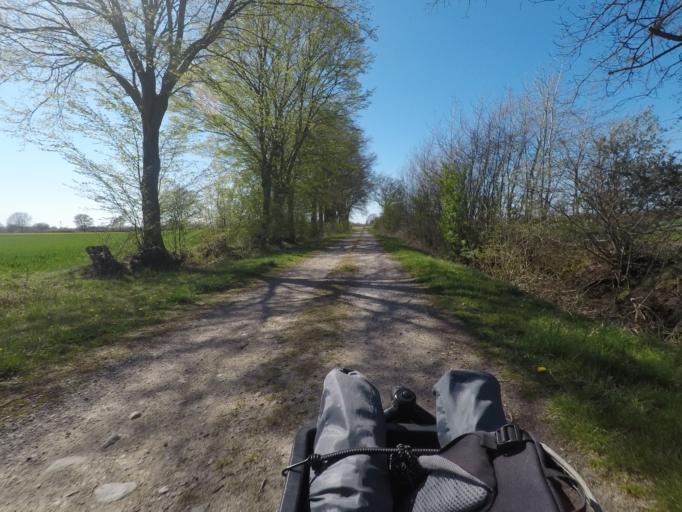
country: DE
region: Schleswig-Holstein
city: Stapelfeld
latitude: 53.6028
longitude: 10.2343
